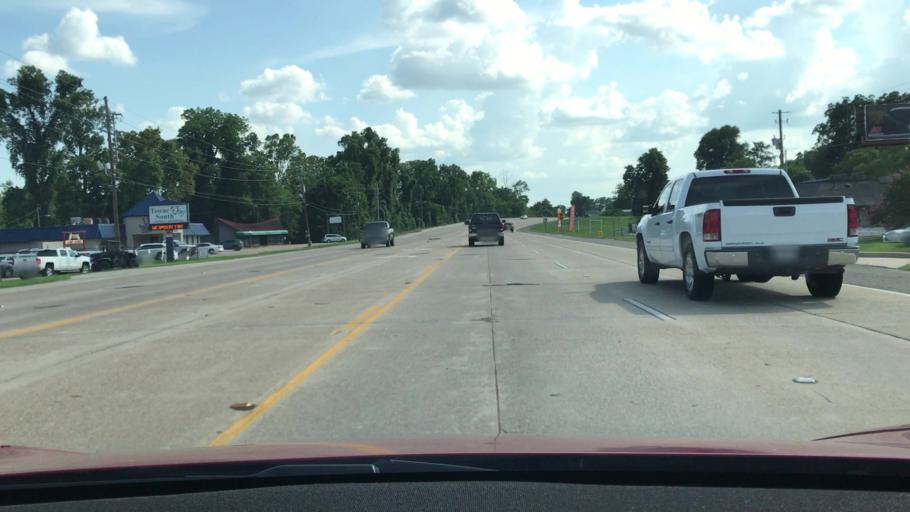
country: US
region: Louisiana
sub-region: Bossier Parish
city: Bossier City
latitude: 32.4487
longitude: -93.6981
